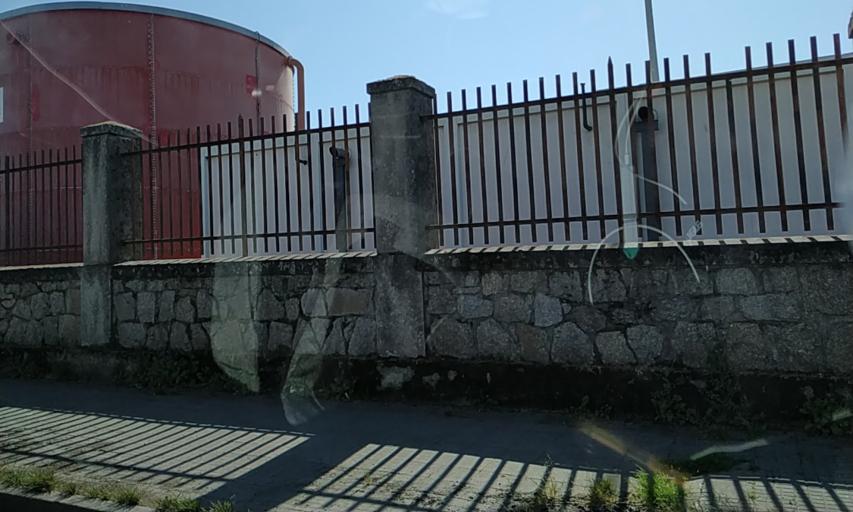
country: ES
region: Galicia
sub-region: Provincia da Coruna
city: A Coruna
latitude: 43.3575
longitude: -8.3957
